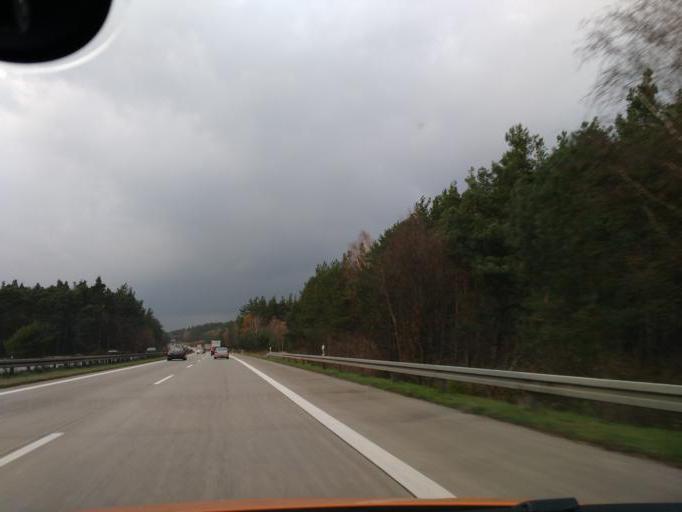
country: DE
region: Brandenburg
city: Heiligengrabe
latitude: 53.1568
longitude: 12.3958
